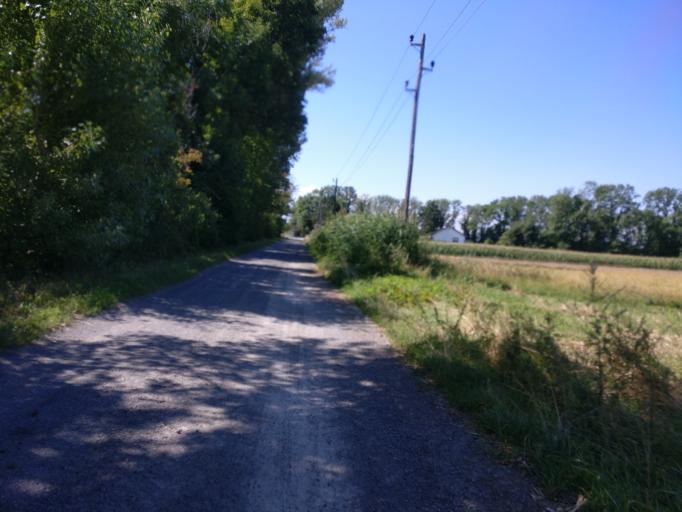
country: AT
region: Lower Austria
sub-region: Politischer Bezirk Baden
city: Pottendorf
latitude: 47.9067
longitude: 16.3520
